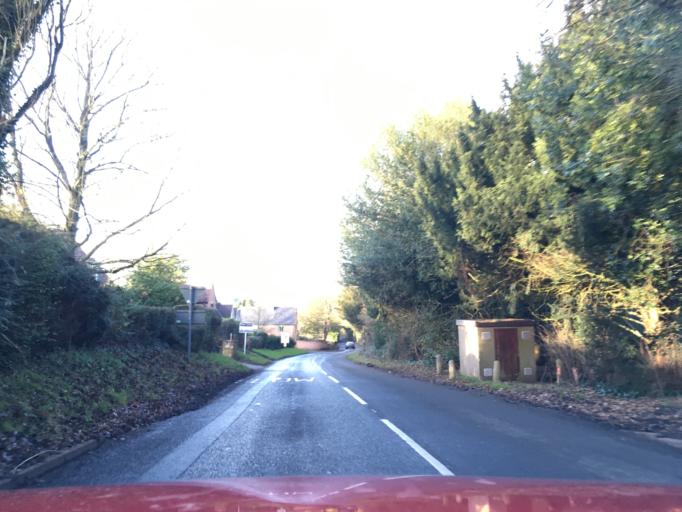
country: GB
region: England
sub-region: Warwickshire
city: Stratford-upon-Avon
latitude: 52.2325
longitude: -1.6844
